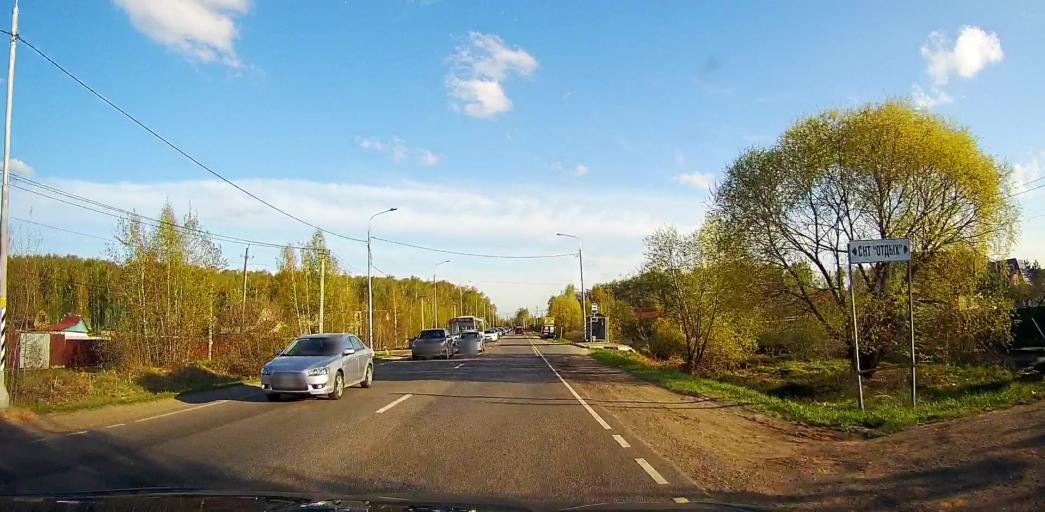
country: RU
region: Moskovskaya
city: Bronnitsy
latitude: 55.3836
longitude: 38.2072
